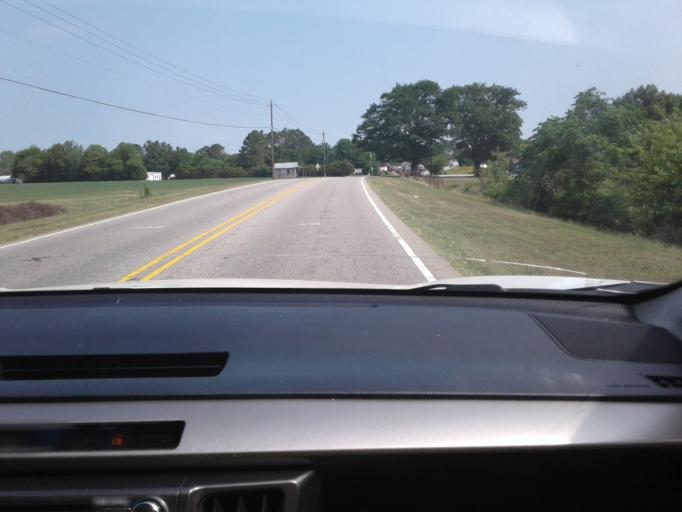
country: US
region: North Carolina
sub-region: Harnett County
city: Coats
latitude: 35.3976
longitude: -78.6724
